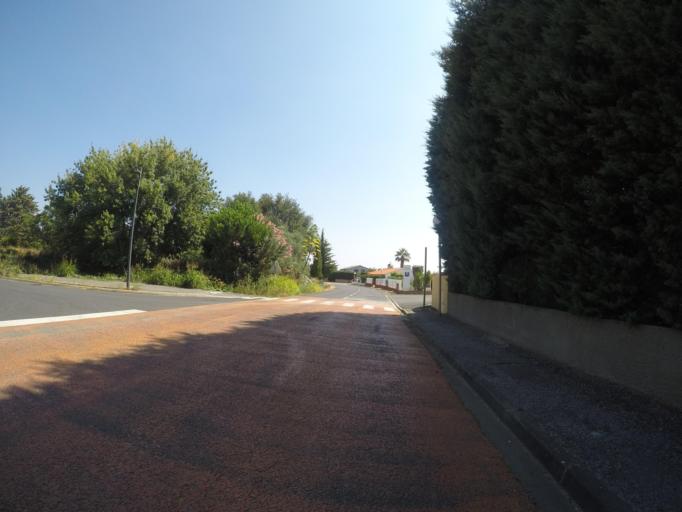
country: FR
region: Languedoc-Roussillon
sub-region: Departement des Pyrenees-Orientales
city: Millas
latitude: 42.6843
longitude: 2.6884
